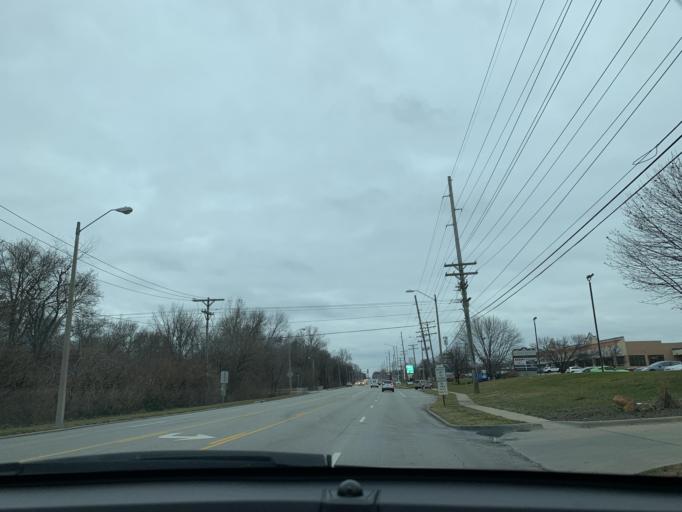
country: US
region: Illinois
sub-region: Sangamon County
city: Jerome
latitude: 39.7719
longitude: -89.6870
